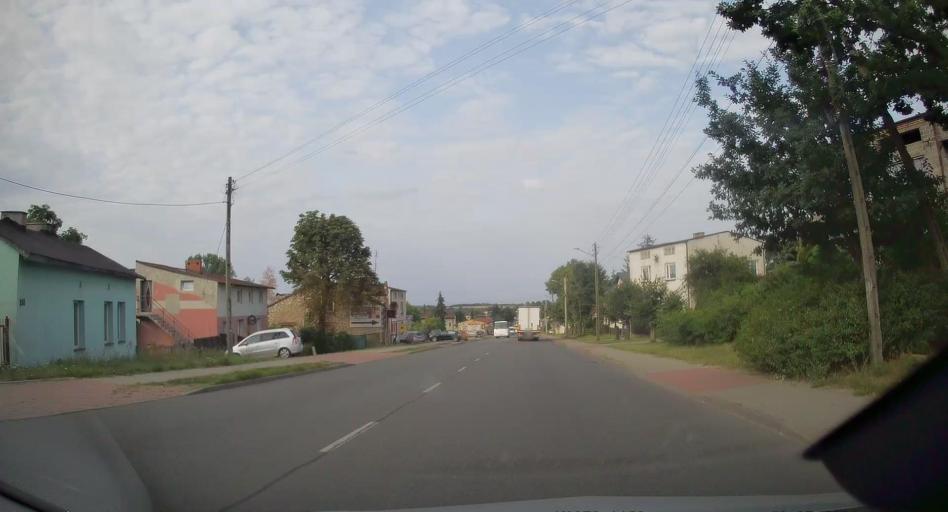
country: PL
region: Silesian Voivodeship
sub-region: Powiat czestochowski
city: Redziny
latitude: 50.8593
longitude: 19.2172
